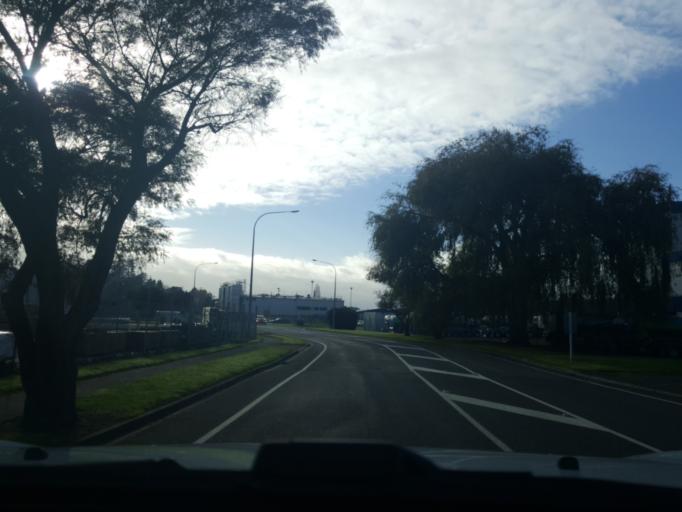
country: NZ
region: Waikato
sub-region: Waipa District
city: Cambridge
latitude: -37.6582
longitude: 175.5319
